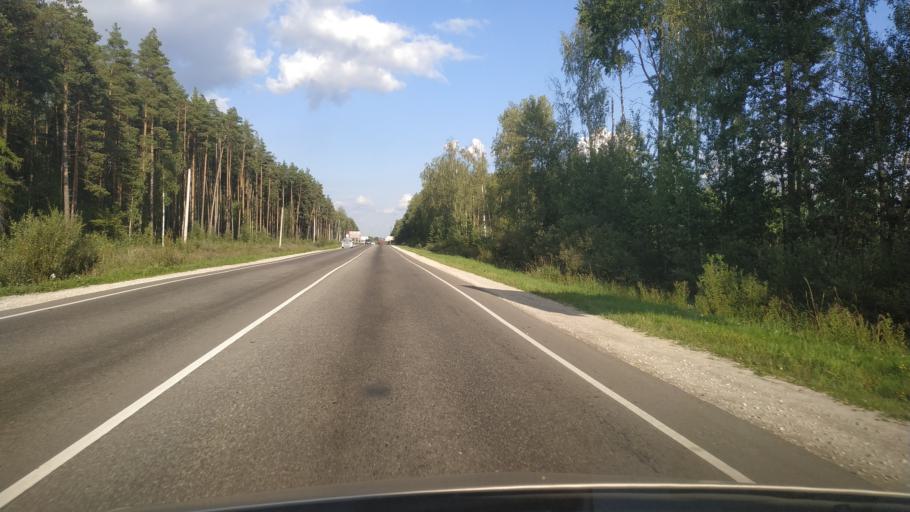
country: RU
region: Moskovskaya
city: Shaturtorf
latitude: 55.5786
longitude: 39.4457
